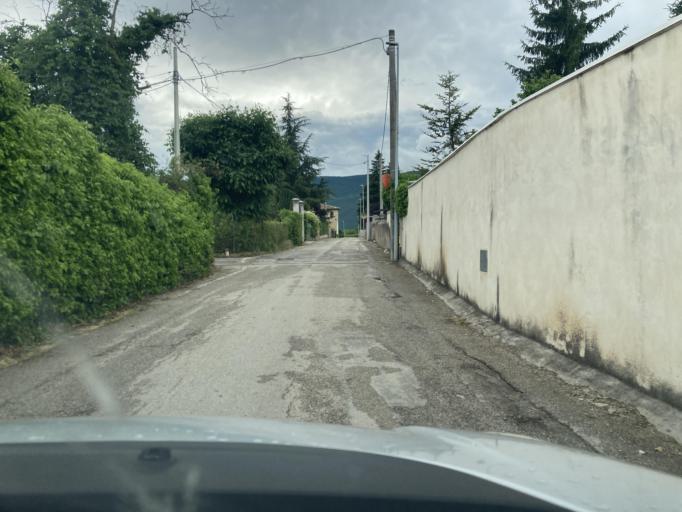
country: IT
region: Abruzzo
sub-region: Provincia dell' Aquila
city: San Demetrio Ne' Vestini
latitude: 42.2926
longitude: 13.5585
